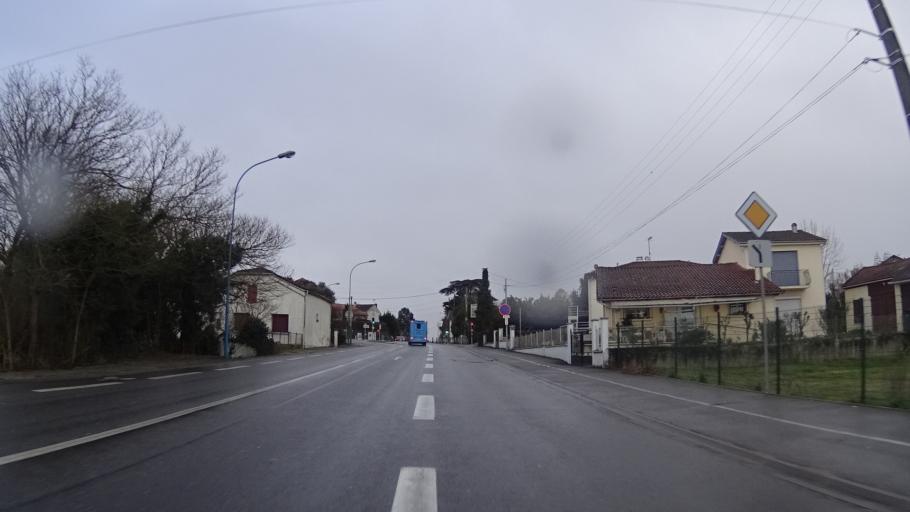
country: FR
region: Aquitaine
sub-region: Departement du Lot-et-Garonne
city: Le Passage
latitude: 44.1889
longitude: 0.6024
